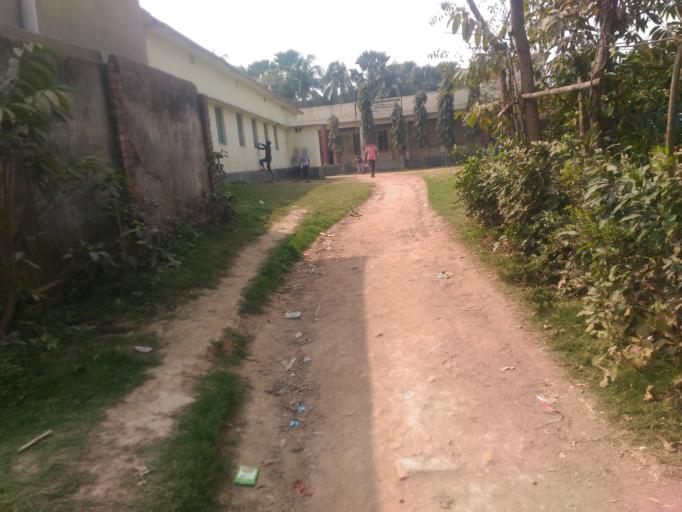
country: BD
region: Dhaka
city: Narayanganj
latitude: 23.6399
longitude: 90.4377
